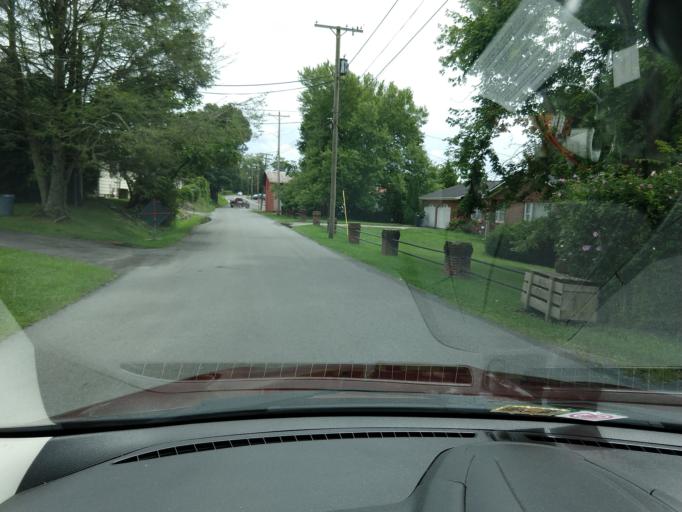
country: US
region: West Virginia
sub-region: Fayette County
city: Oak Hill
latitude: 37.9728
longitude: -81.1538
